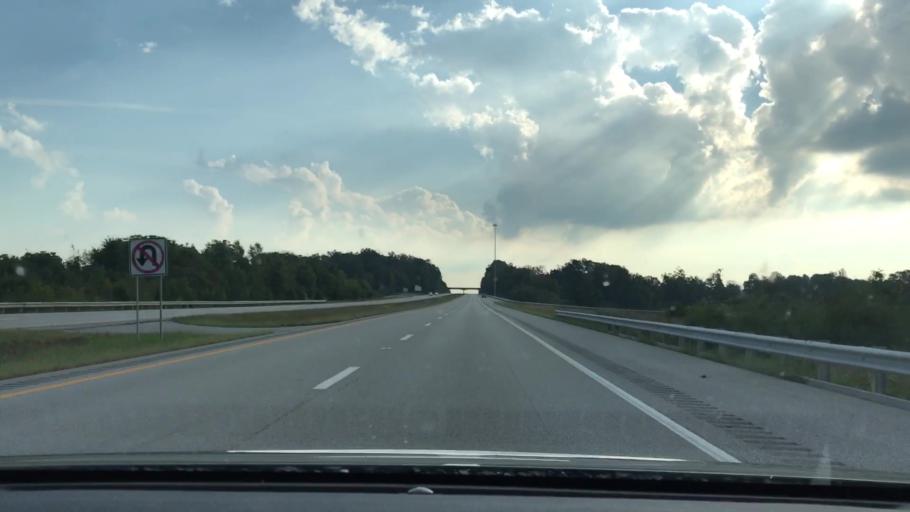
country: US
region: Kentucky
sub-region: Barren County
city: Glasgow
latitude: 36.9945
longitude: -85.8738
